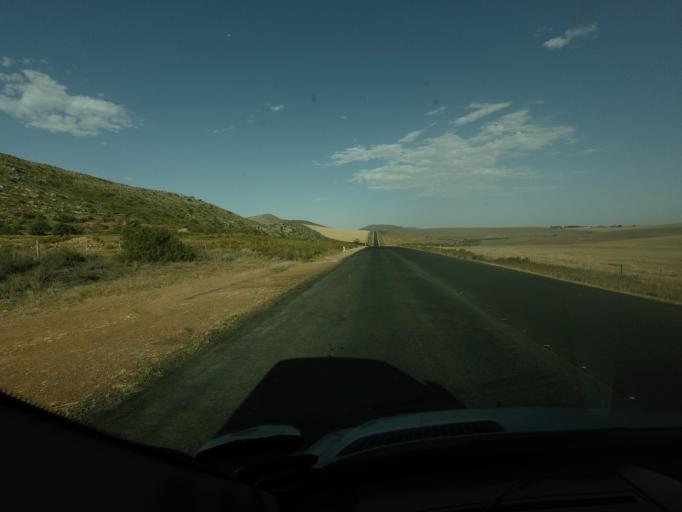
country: ZA
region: Western Cape
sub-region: Overberg District Municipality
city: Swellendam
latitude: -34.1018
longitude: 20.2212
